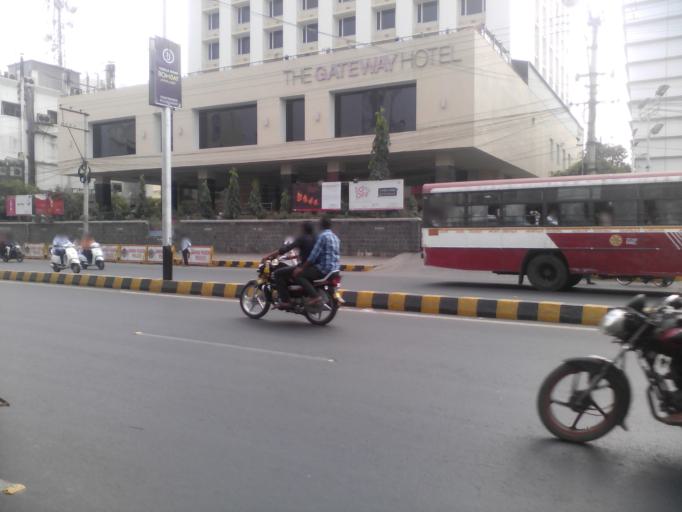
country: IN
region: Andhra Pradesh
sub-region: Krishna
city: Vijayawada
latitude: 16.5032
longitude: 80.6405
